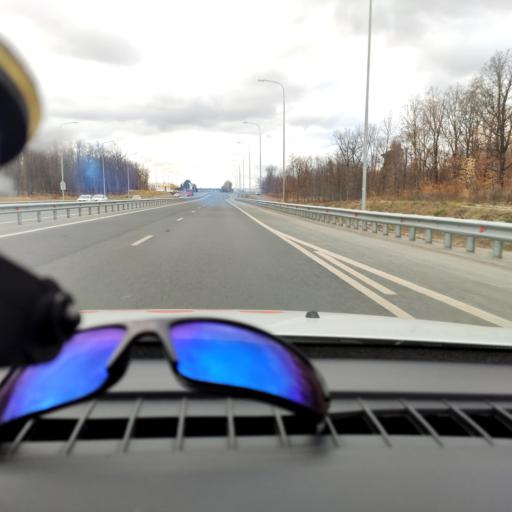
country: RU
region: Samara
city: Bereza
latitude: 53.5087
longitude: 50.1381
